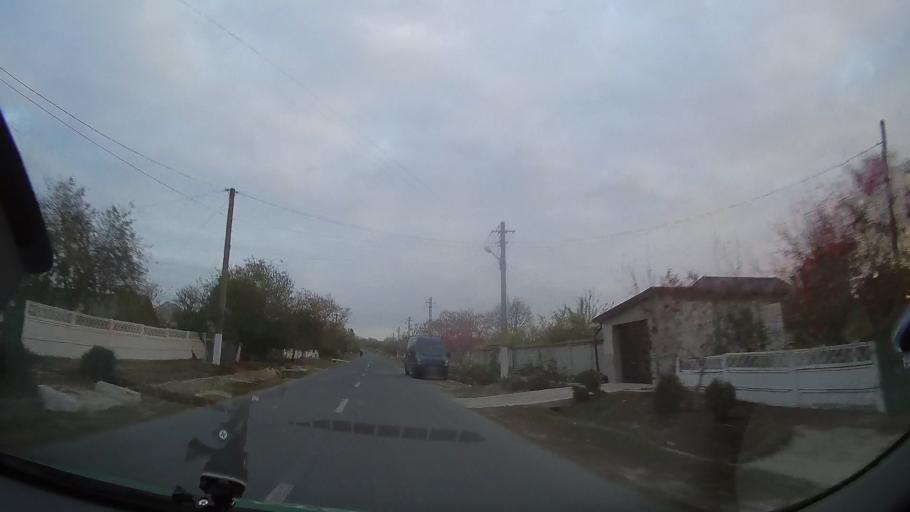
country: RO
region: Tulcea
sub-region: Comuna Mihai Bravu
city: Turda
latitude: 44.9810
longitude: 28.6157
